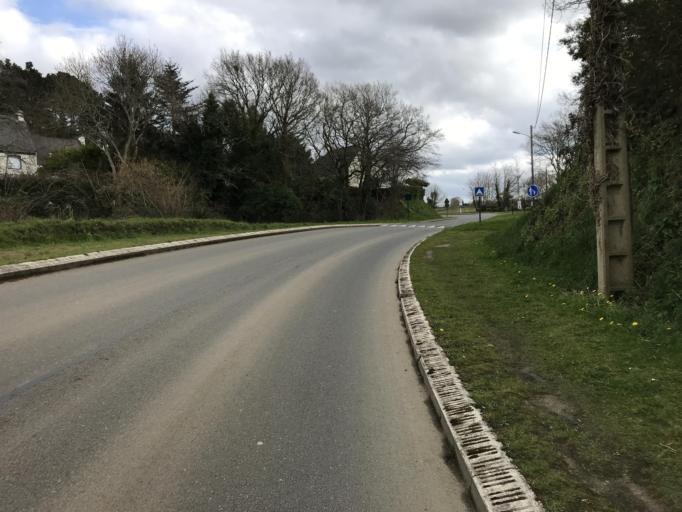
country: FR
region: Brittany
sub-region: Departement du Finistere
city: Hopital-Camfrout
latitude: 48.3270
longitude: -4.2351
